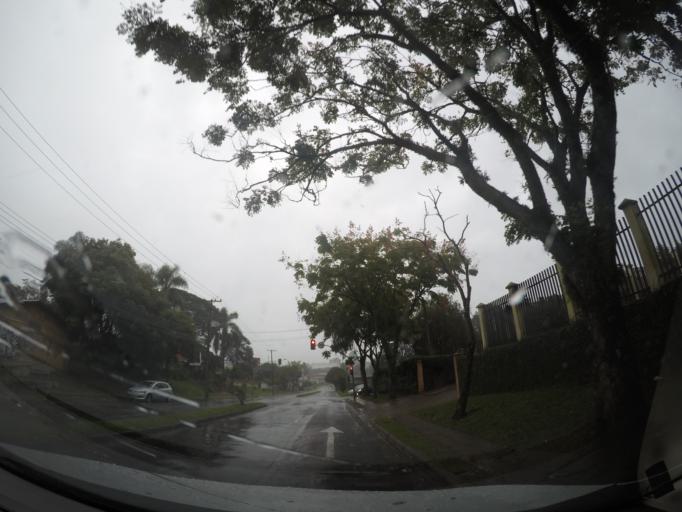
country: BR
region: Parana
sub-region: Curitiba
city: Curitiba
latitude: -25.4506
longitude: -49.3551
